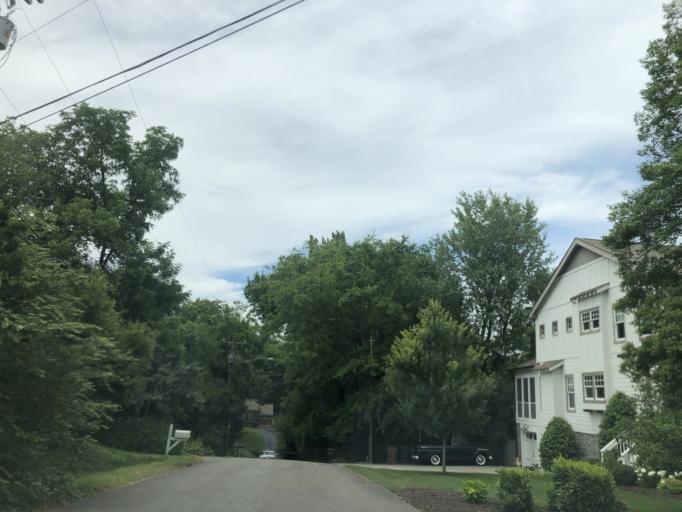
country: US
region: Tennessee
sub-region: Davidson County
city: Oak Hill
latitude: 36.1065
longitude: -86.7840
